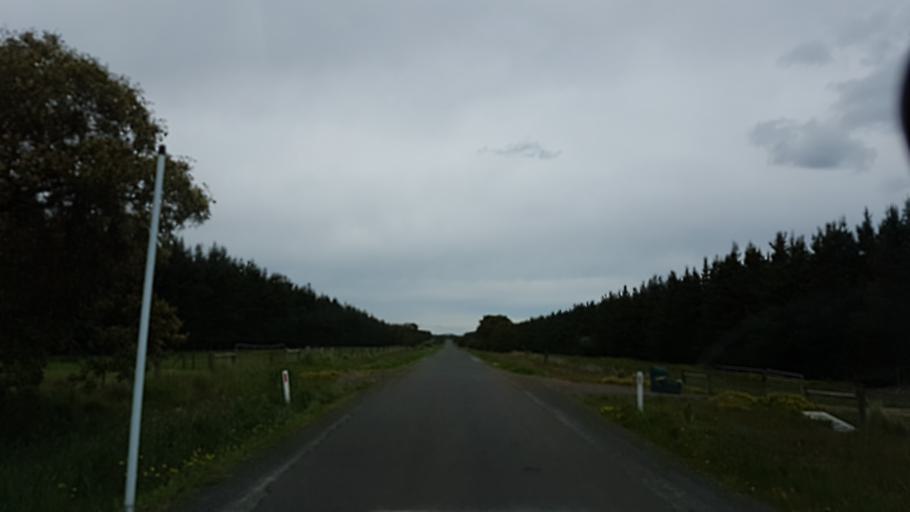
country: AU
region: Victoria
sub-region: Ballarat North
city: Mount Clear
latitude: -37.7829
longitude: 144.1299
